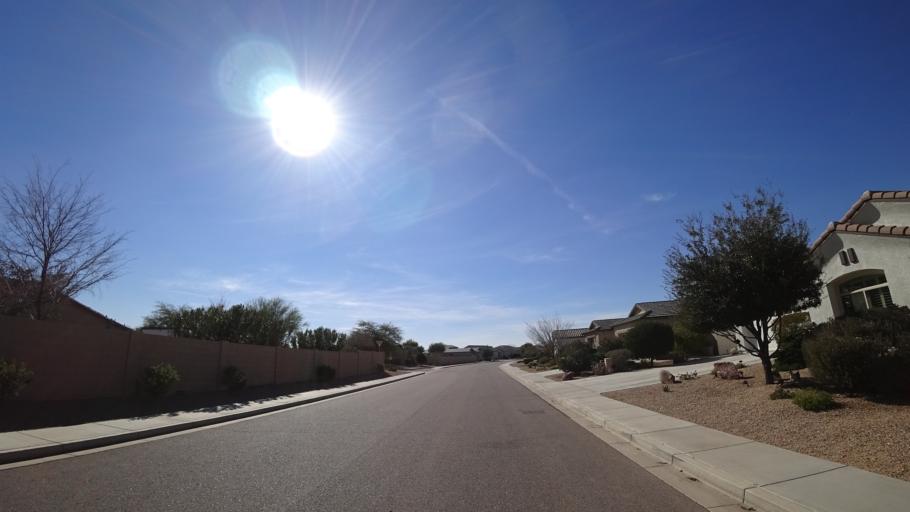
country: US
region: Arizona
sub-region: Maricopa County
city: Citrus Park
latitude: 33.5128
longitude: -112.4559
